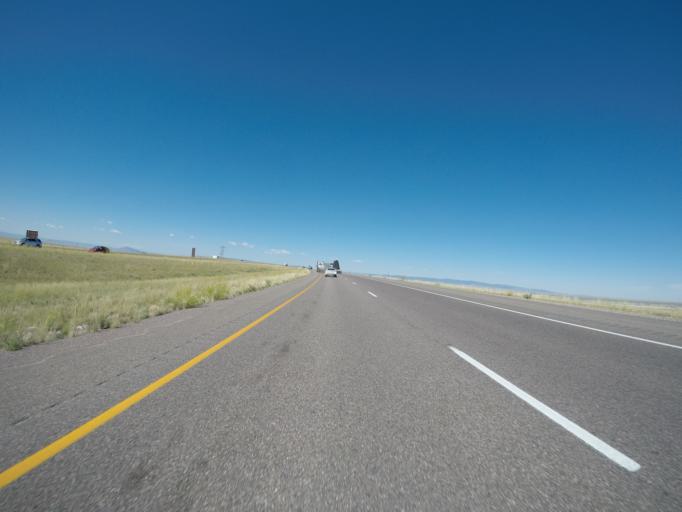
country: US
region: Wyoming
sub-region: Albany County
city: Laramie
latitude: 41.3507
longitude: -105.6968
